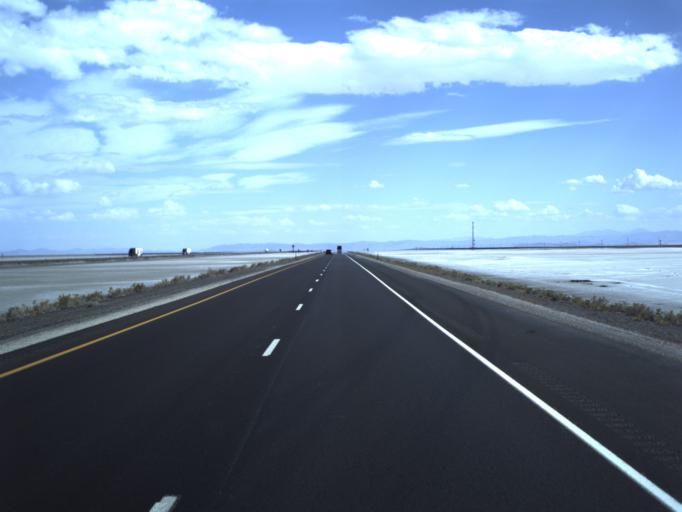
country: US
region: Utah
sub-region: Tooele County
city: Wendover
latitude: 40.7330
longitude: -113.5921
